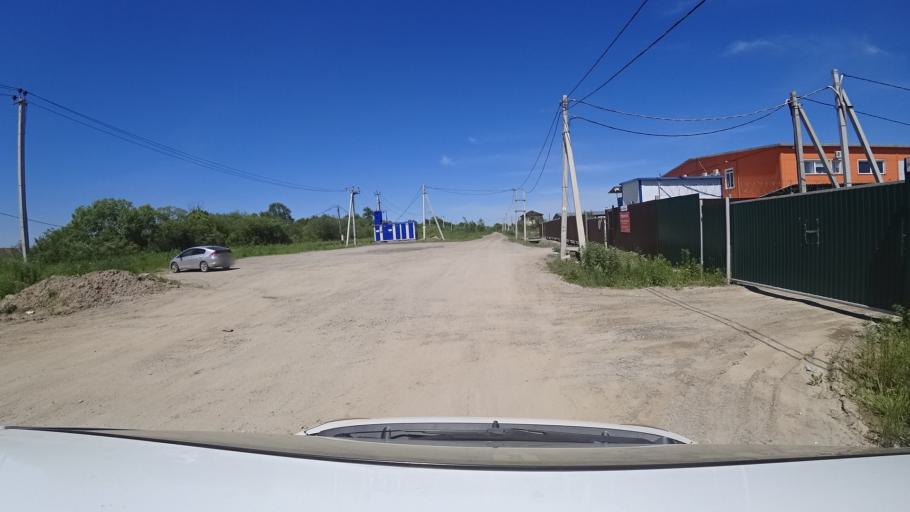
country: RU
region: Khabarovsk Krai
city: Topolevo
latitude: 48.4824
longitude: 135.1747
